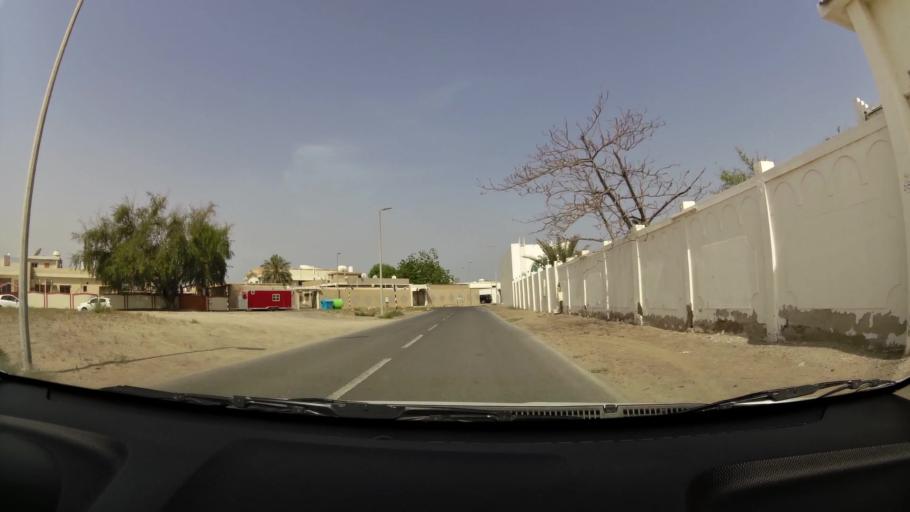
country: AE
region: Ash Shariqah
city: Sharjah
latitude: 25.3520
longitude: 55.4157
